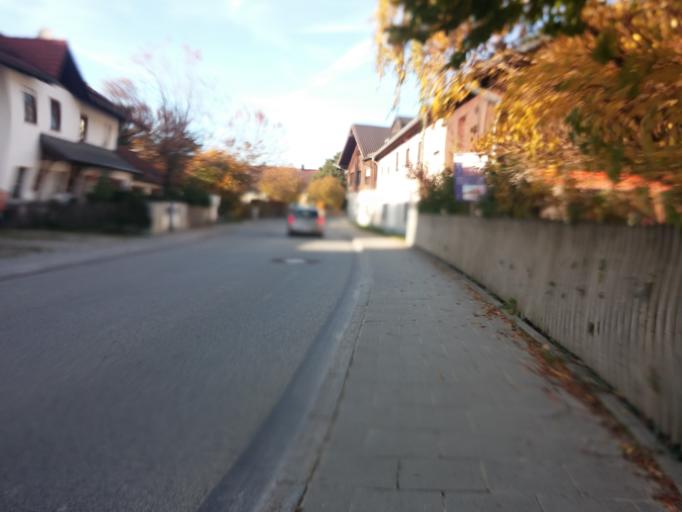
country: DE
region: Bavaria
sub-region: Upper Bavaria
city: Haar
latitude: 48.1293
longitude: 11.7168
